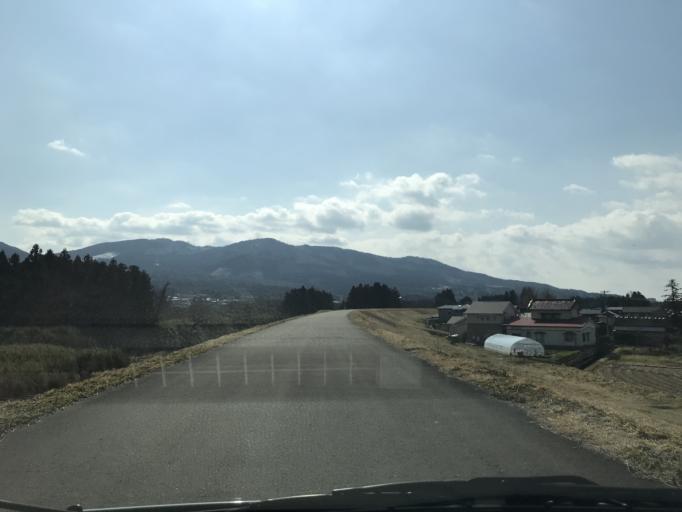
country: JP
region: Iwate
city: Mizusawa
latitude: 39.0504
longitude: 141.1464
